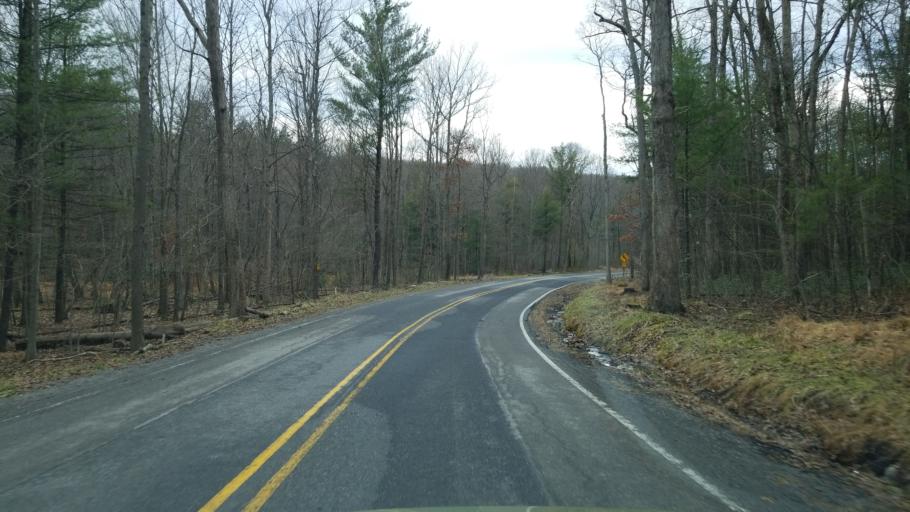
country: US
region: Pennsylvania
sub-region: Clearfield County
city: Clearfield
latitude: 41.0536
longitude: -78.4886
